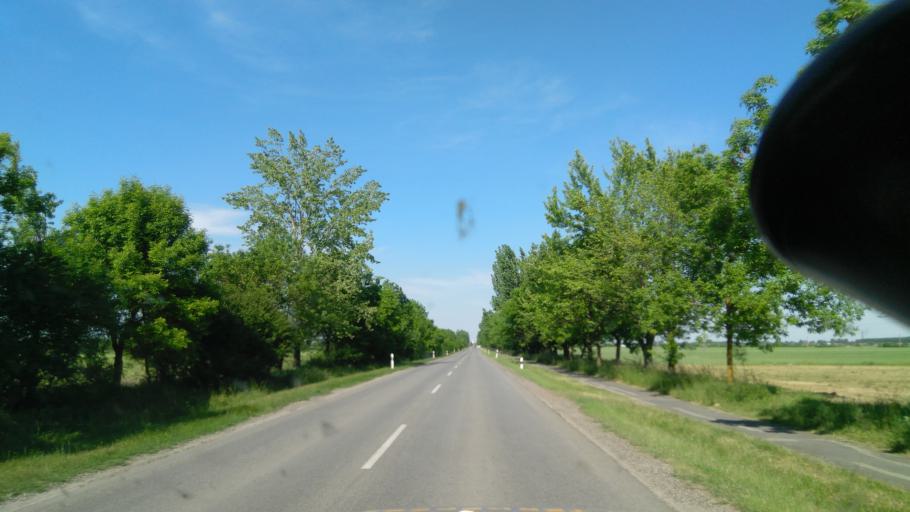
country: HU
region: Bekes
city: Sarkad
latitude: 46.7258
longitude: 21.3434
